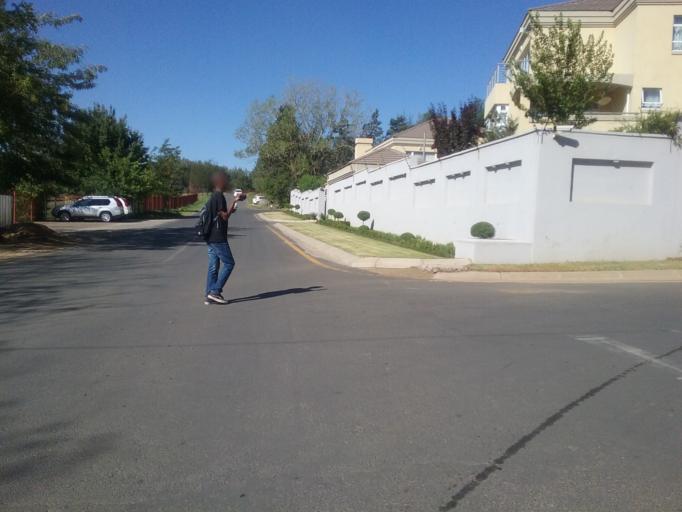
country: LS
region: Maseru
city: Maseru
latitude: -29.3123
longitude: 27.4710
